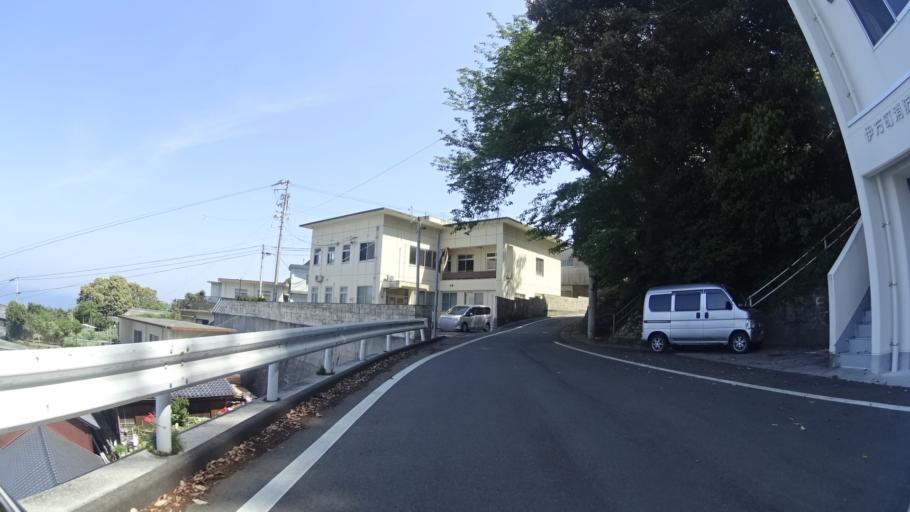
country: JP
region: Ehime
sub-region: Nishiuwa-gun
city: Ikata-cho
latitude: 33.3719
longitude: 132.0530
